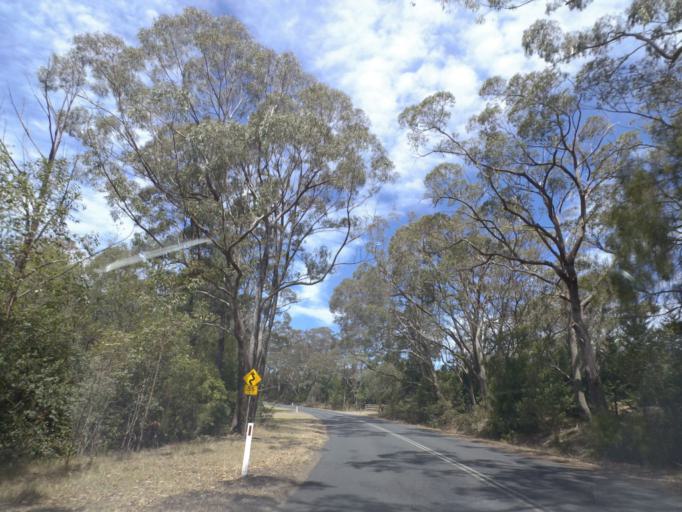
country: AU
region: New South Wales
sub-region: Wingecarribee
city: Colo Vale
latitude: -34.4064
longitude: 150.5107
